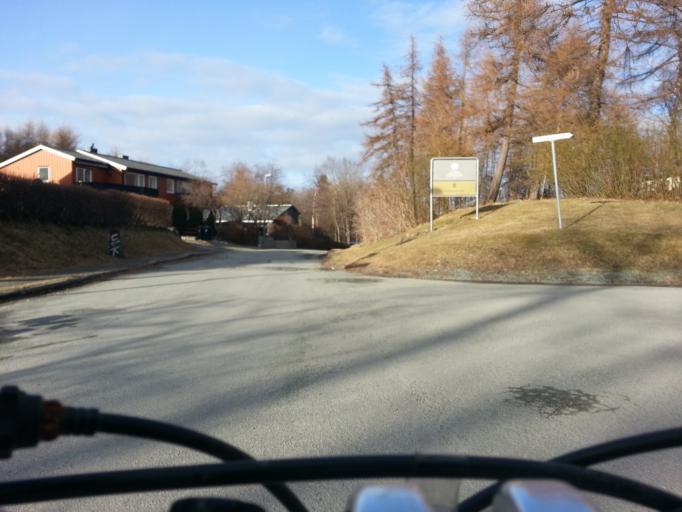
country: NO
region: Sor-Trondelag
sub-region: Trondheim
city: Trondheim
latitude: 63.4541
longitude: 10.4436
